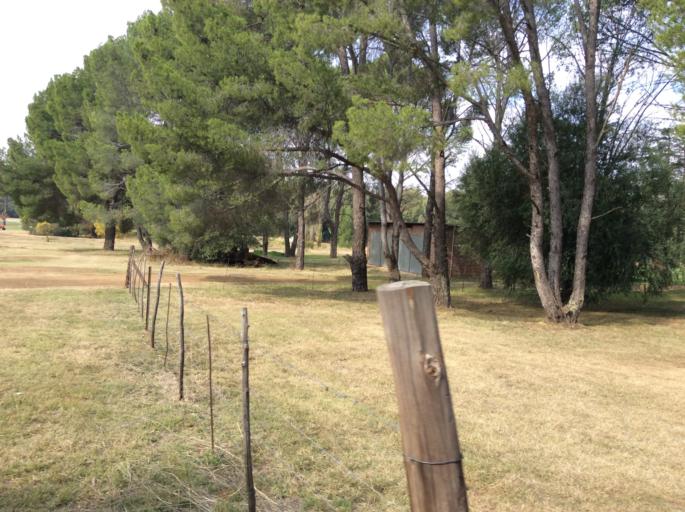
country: ZA
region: Orange Free State
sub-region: Xhariep District Municipality
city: Dewetsdorp
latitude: -29.5758
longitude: 26.6645
